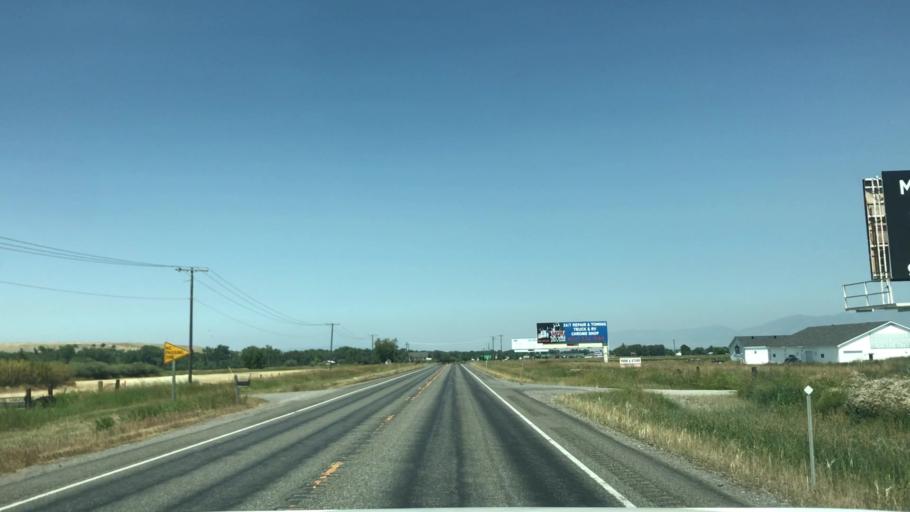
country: US
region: Montana
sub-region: Gallatin County
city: Four Corners
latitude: 45.6348
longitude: -111.1968
